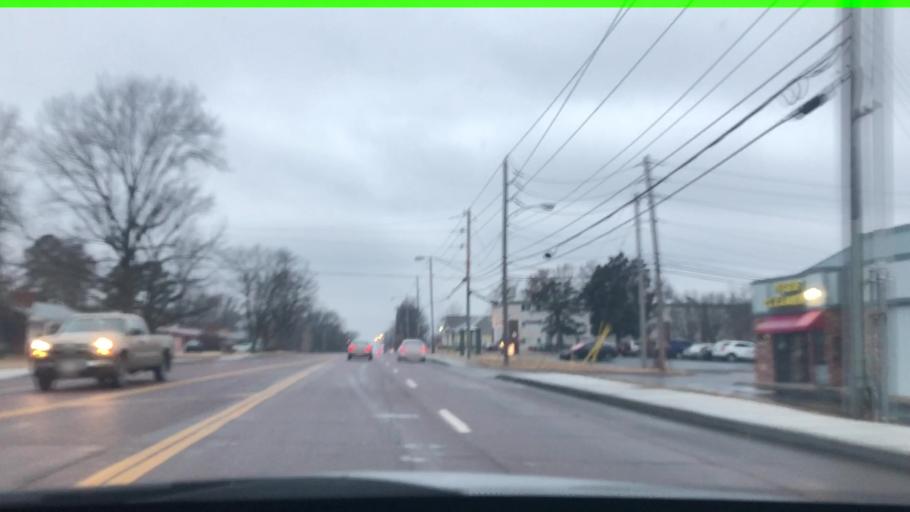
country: US
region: Missouri
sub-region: Boone County
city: Columbia
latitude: 38.9541
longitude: -92.3733
